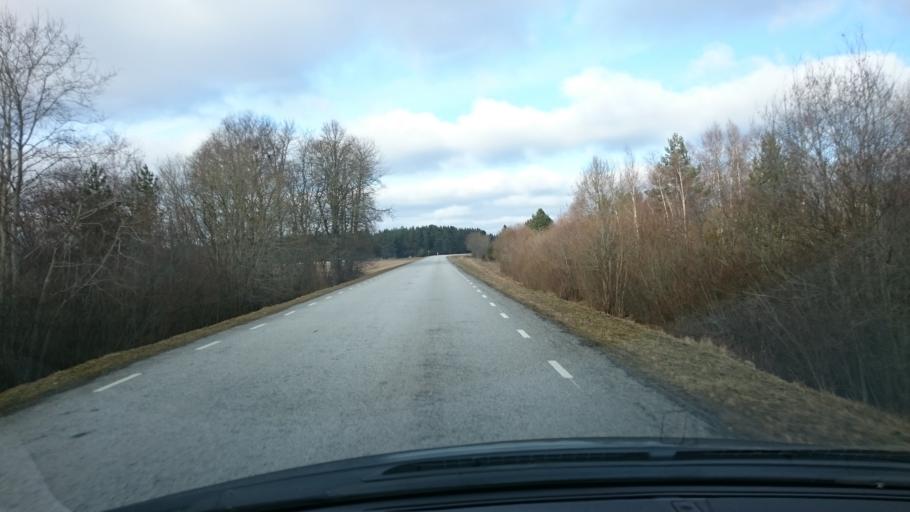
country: EE
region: Harju
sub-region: Keila linn
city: Keila
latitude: 59.3554
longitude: 24.3439
